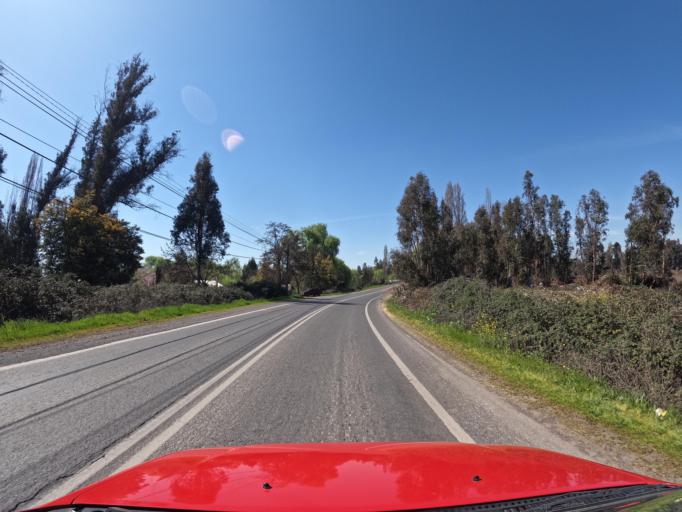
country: CL
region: Maule
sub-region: Provincia de Curico
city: Rauco
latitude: -34.9947
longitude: -71.3512
